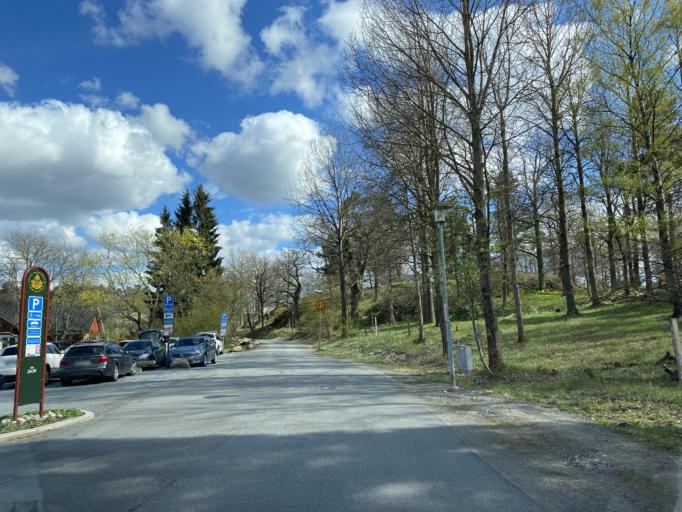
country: SE
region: Stockholm
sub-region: Stockholms Kommun
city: OEstermalm
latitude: 59.3643
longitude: 18.0708
